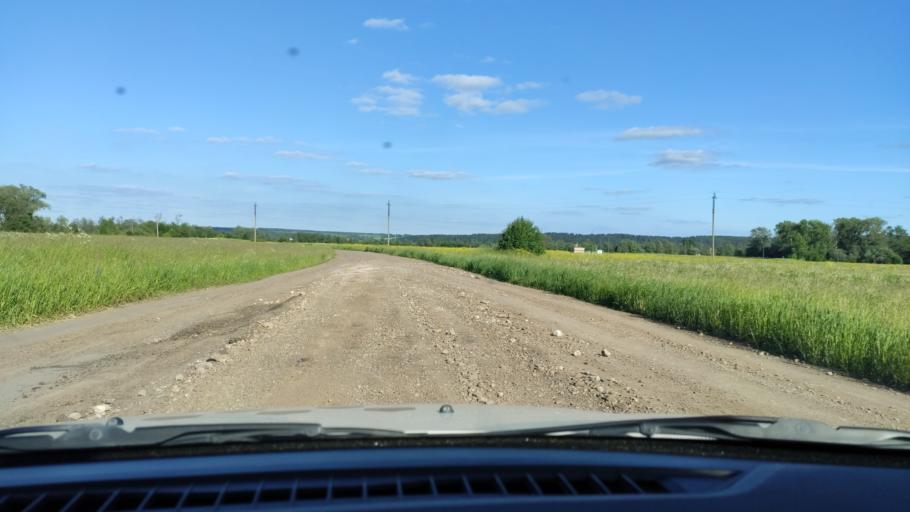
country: RU
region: Perm
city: Orda
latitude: 57.3010
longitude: 56.6210
